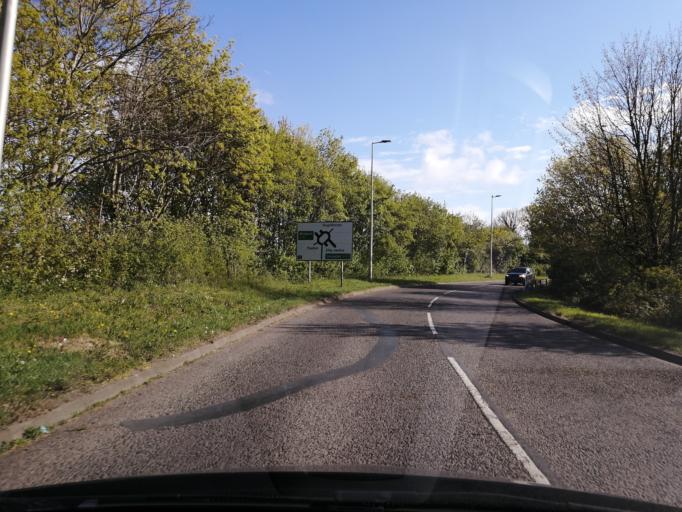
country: GB
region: England
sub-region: Peterborough
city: Peterborough
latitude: 52.6030
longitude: -0.2487
